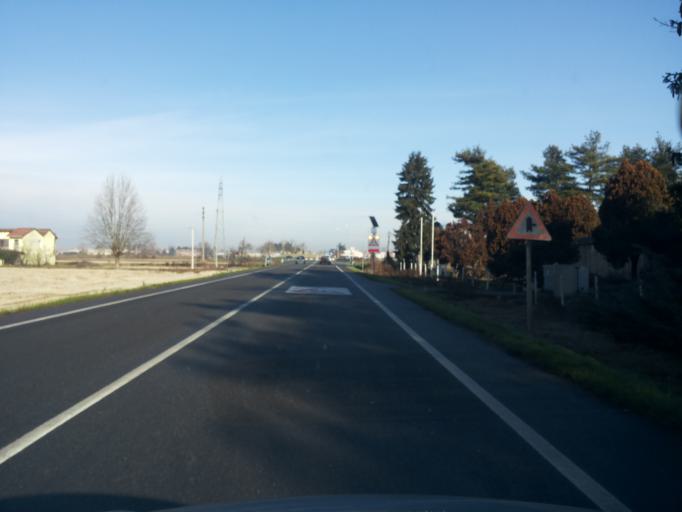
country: IT
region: Piedmont
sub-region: Provincia di Vercelli
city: Caresanablot
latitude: 45.3396
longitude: 8.3935
